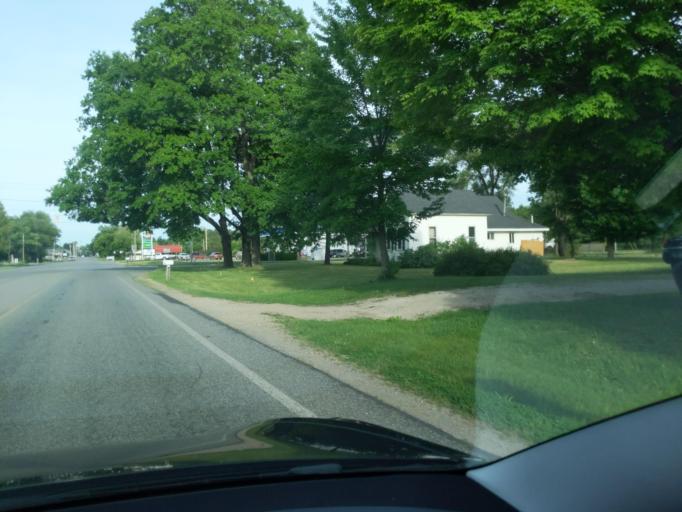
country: US
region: Michigan
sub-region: Montcalm County
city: Howard City
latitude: 43.3957
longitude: -85.4778
